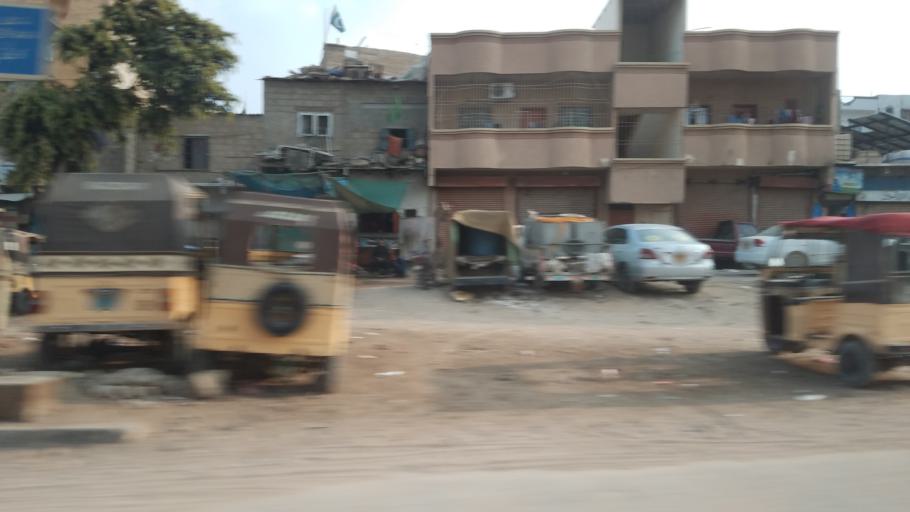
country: PK
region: Sindh
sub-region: Karachi District
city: Karachi
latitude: 24.9282
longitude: 67.0884
